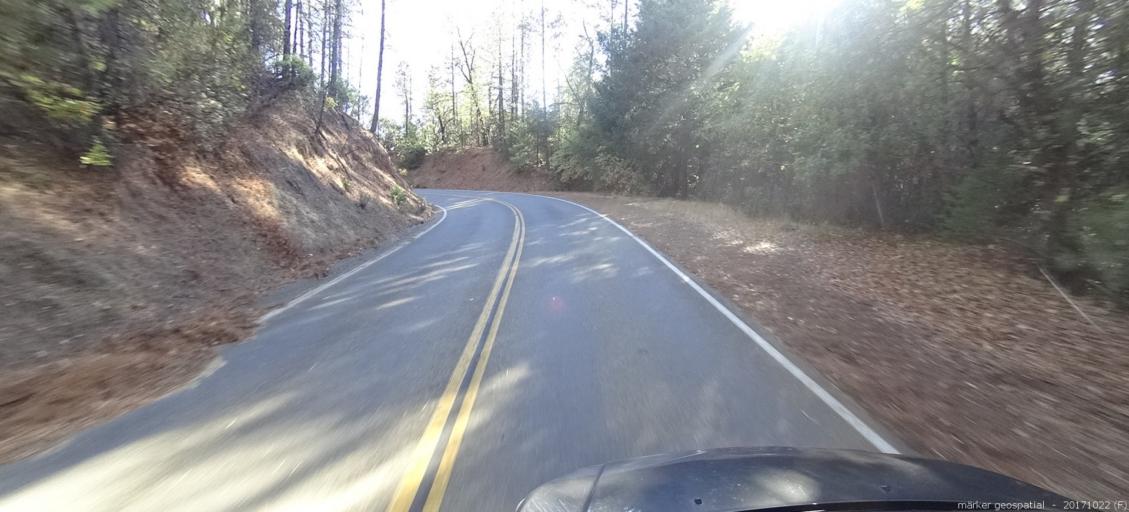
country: US
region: California
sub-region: Shasta County
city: Shasta Lake
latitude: 40.8740
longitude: -122.2631
